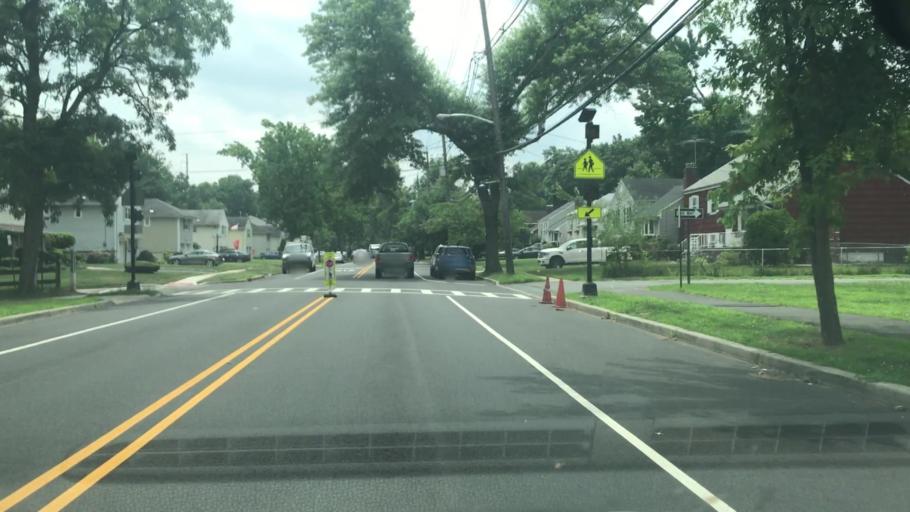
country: US
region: New Jersey
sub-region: Union County
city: Clark
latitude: 40.6450
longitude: -74.3048
